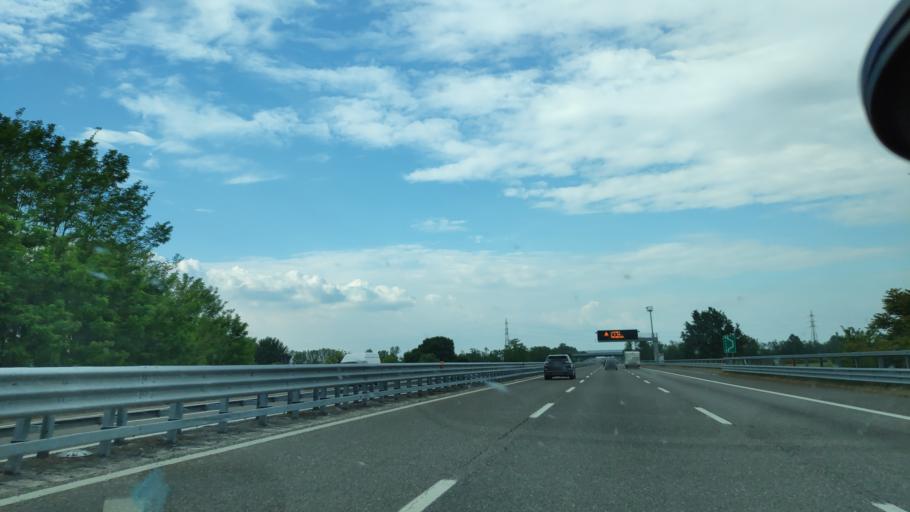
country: IT
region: Lombardy
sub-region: Provincia di Pavia
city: Gropello Cairoli
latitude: 45.1598
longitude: 8.9976
